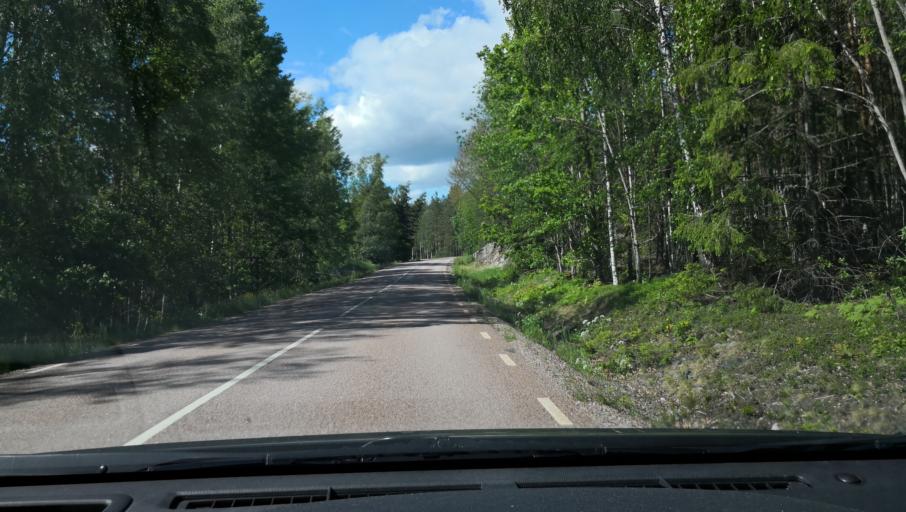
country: SE
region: Vaestmanland
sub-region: Arboga Kommun
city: Tyringe
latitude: 59.3027
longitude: 16.0167
